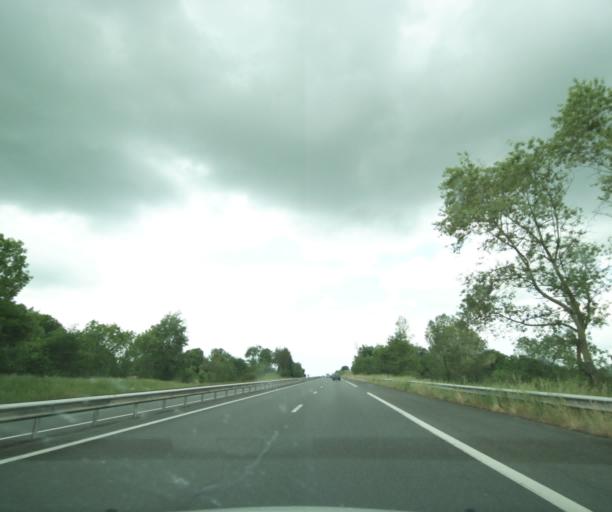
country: FR
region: Auvergne
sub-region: Departement de l'Allier
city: Montmarault
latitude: 46.3375
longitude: 2.8852
